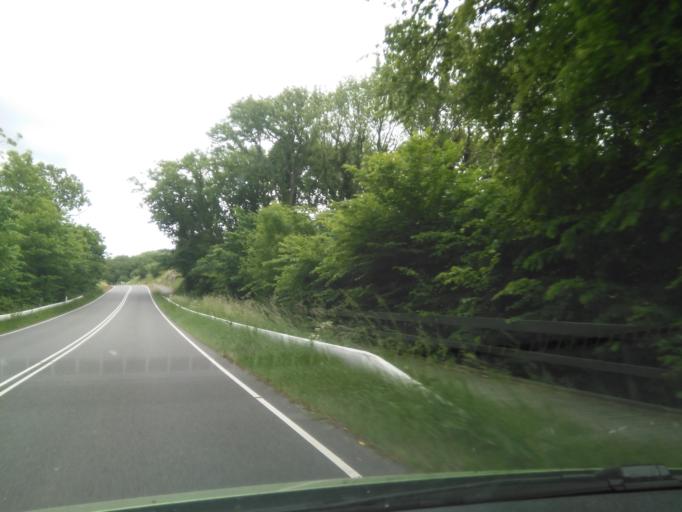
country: DK
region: Capital Region
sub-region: Bornholm Kommune
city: Akirkeby
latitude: 55.2243
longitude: 14.8902
